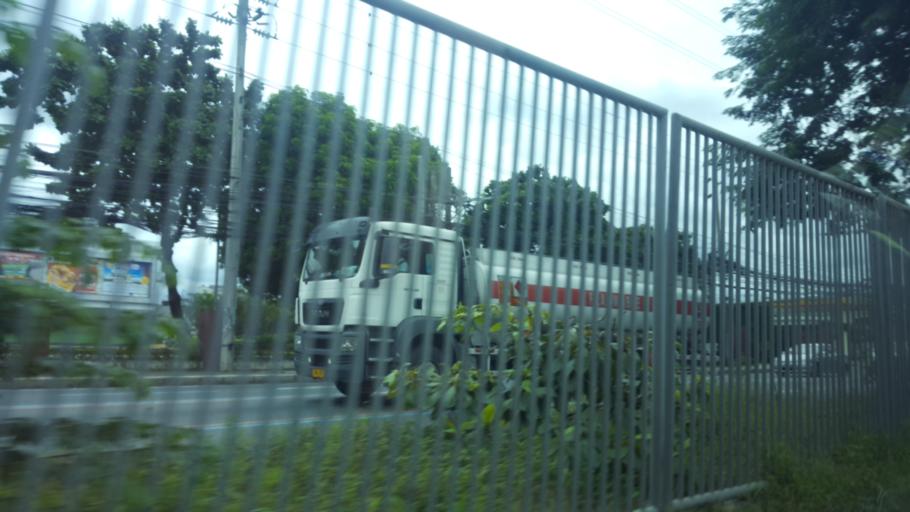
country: PH
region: Metro Manila
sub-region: Marikina
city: Calumpang
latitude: 14.6034
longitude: 121.0792
